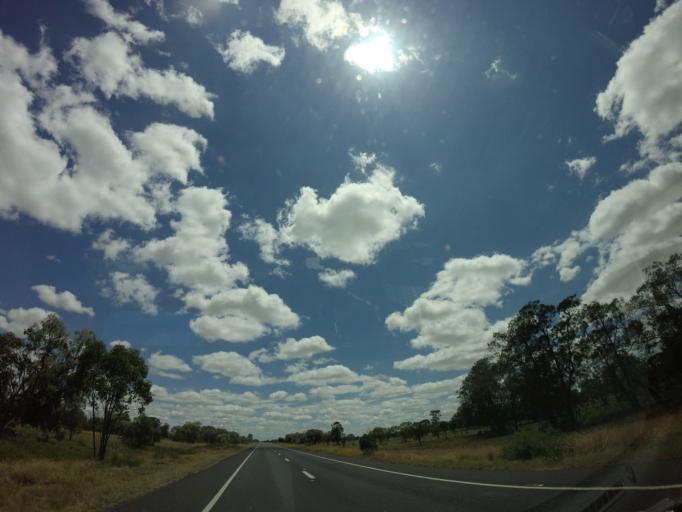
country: AU
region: New South Wales
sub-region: Moree Plains
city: Moree
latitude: -29.1036
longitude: 150.0313
